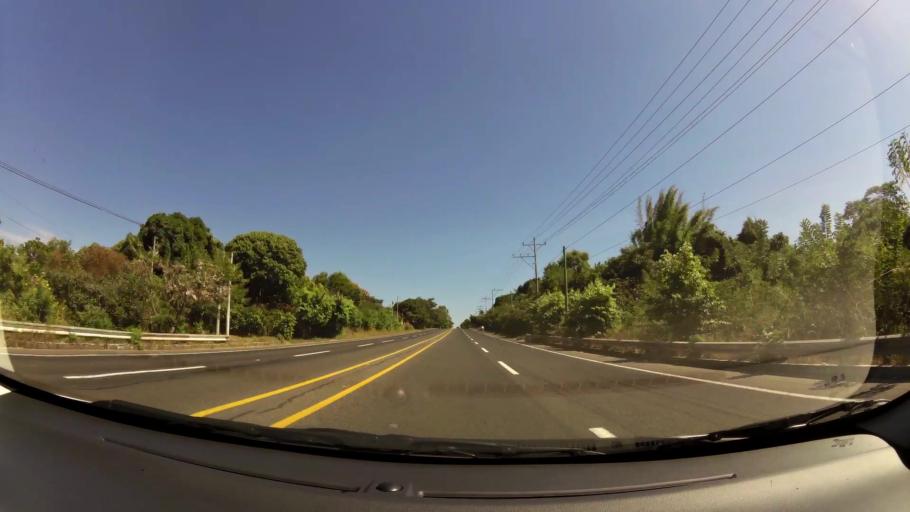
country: SV
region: Ahuachapan
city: Atiquizaya
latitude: 13.9711
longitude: -89.7475
